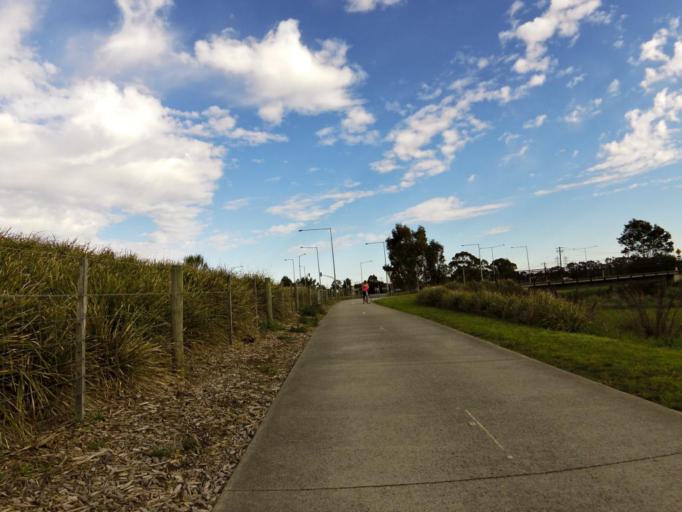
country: AU
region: Victoria
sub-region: Knox
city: Wantirna South
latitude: -37.9023
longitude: 145.2143
